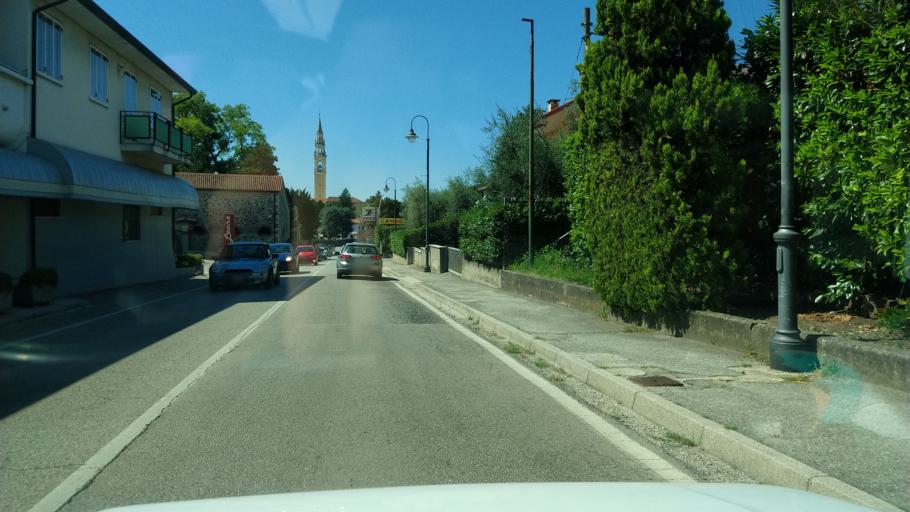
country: IT
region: Veneto
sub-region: Provincia di Vicenza
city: Mason Vicentino
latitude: 45.7210
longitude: 11.6096
